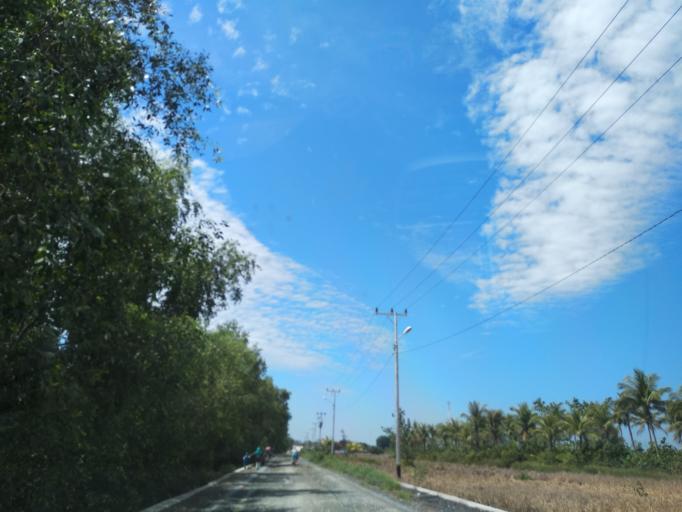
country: ID
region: South Kalimantan
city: Tabunganen
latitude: -3.4043
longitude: 114.4908
